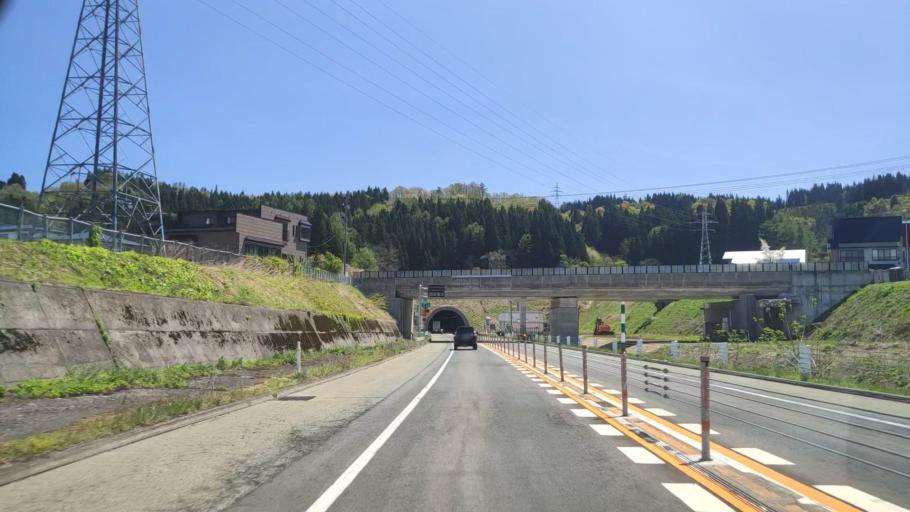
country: JP
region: Yamagata
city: Shinjo
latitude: 38.6907
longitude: 140.3125
